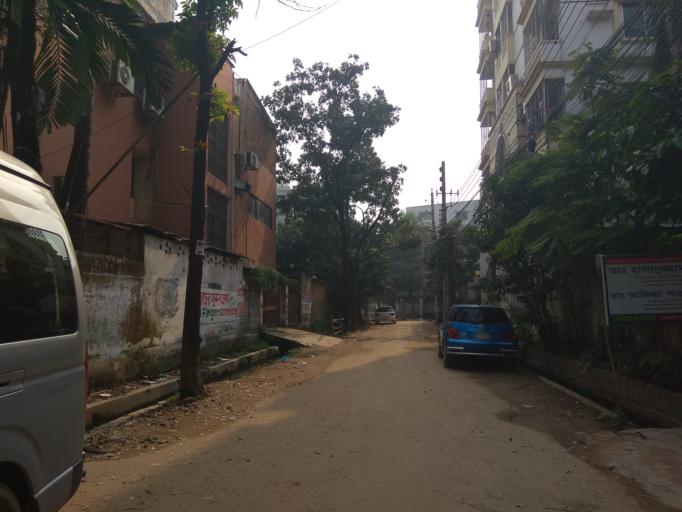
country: BD
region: Dhaka
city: Tungi
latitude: 23.8734
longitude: 90.3993
